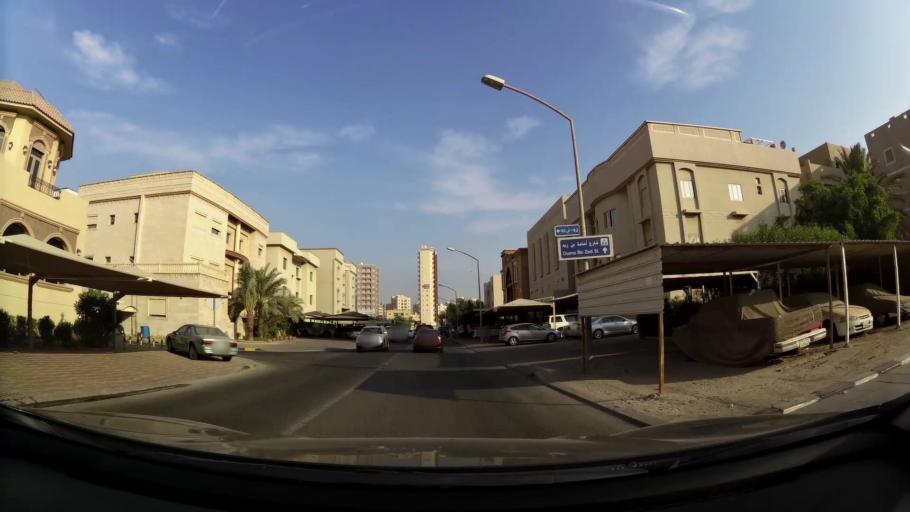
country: KW
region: Muhafazat Hawalli
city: Ar Rumaythiyah
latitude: 29.3228
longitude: 48.0722
